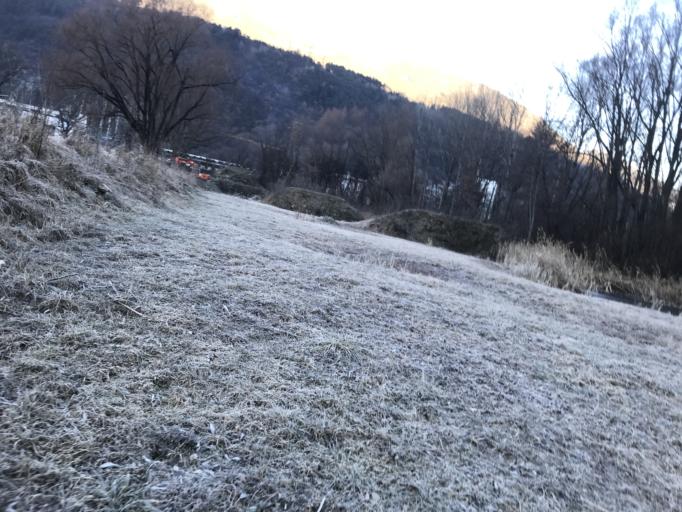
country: IT
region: Trentino-Alto Adige
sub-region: Bolzano
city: Bressanone
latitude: 46.6998
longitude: 11.6524
